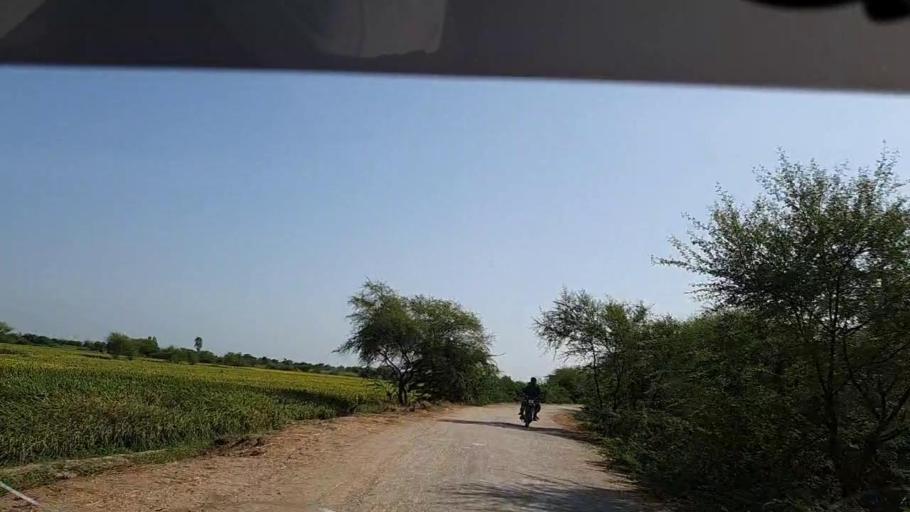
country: PK
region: Sindh
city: Badin
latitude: 24.6403
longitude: 68.7874
